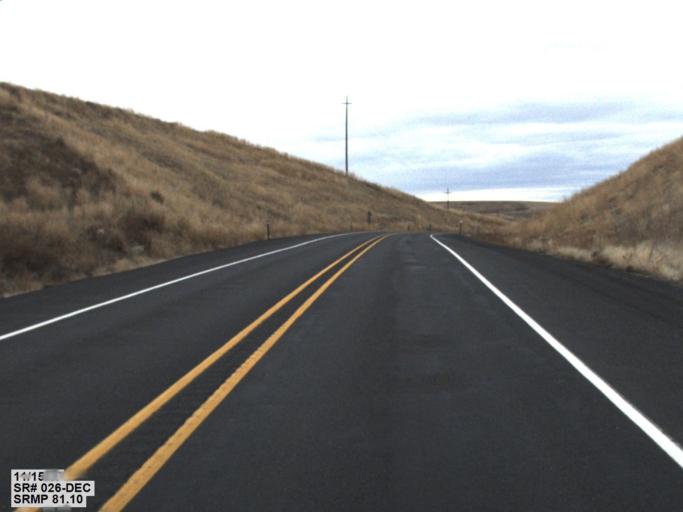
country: US
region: Washington
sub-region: Adams County
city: Ritzville
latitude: 46.7672
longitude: -118.3447
